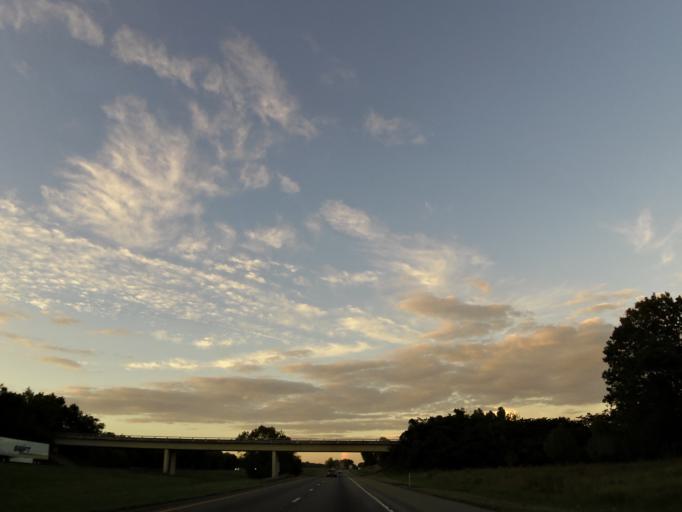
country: US
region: Tennessee
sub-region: McMinn County
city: Athens
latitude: 35.5393
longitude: -84.5750
